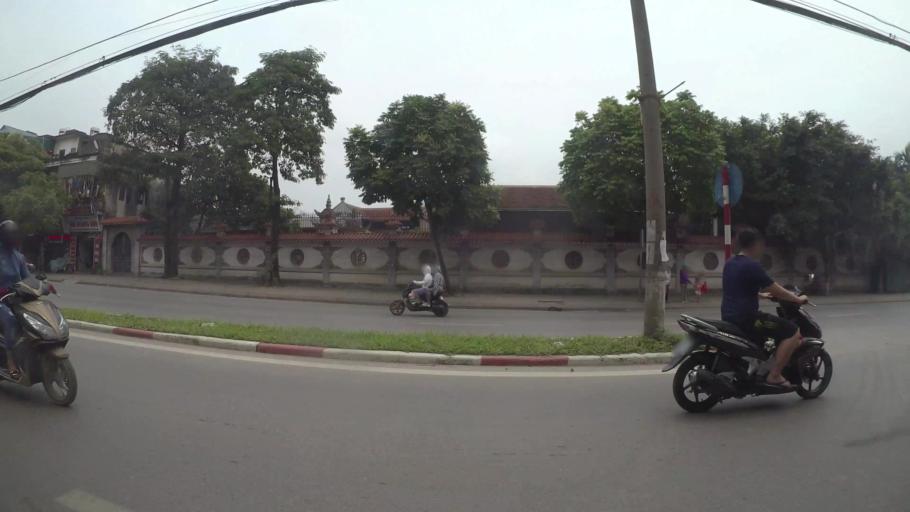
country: VN
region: Ha Noi
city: Ha Dong
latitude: 20.9797
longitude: 105.7722
